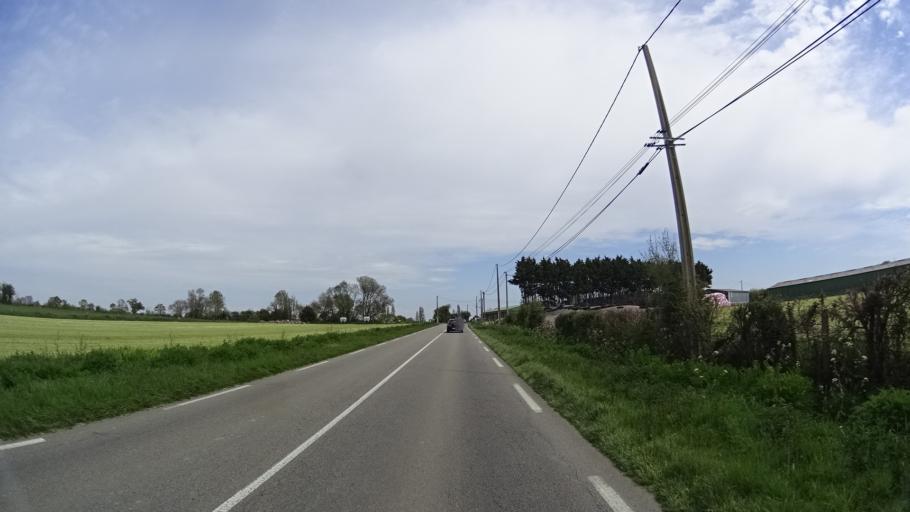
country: FR
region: Pays de la Loire
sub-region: Departement de la Loire-Atlantique
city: Port-Saint-Pere
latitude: 47.1140
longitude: -1.7768
